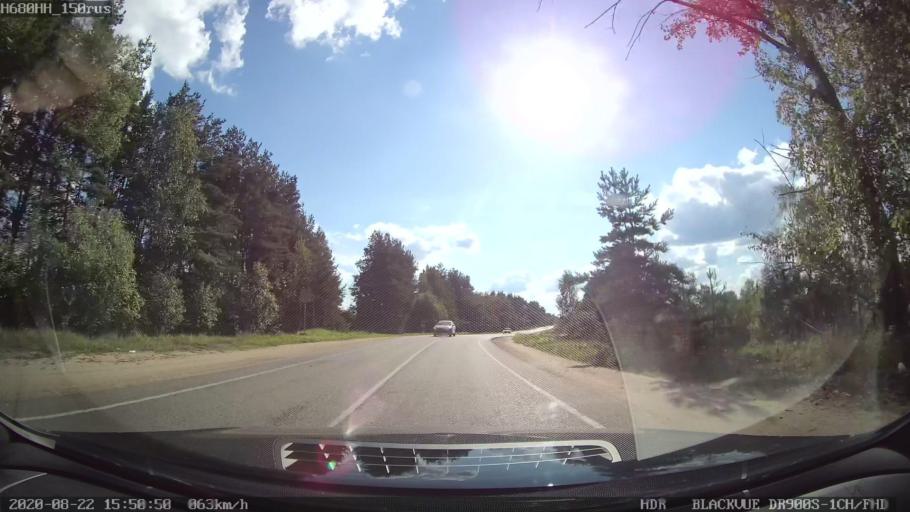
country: RU
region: Tverskaya
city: Bezhetsk
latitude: 57.6686
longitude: 36.4372
